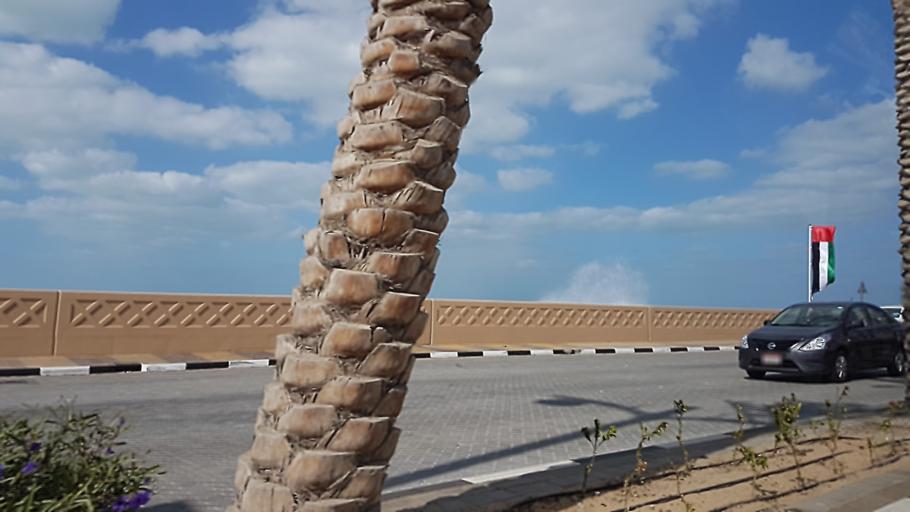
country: AE
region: Dubai
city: Dubai
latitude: 25.1269
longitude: 55.1126
